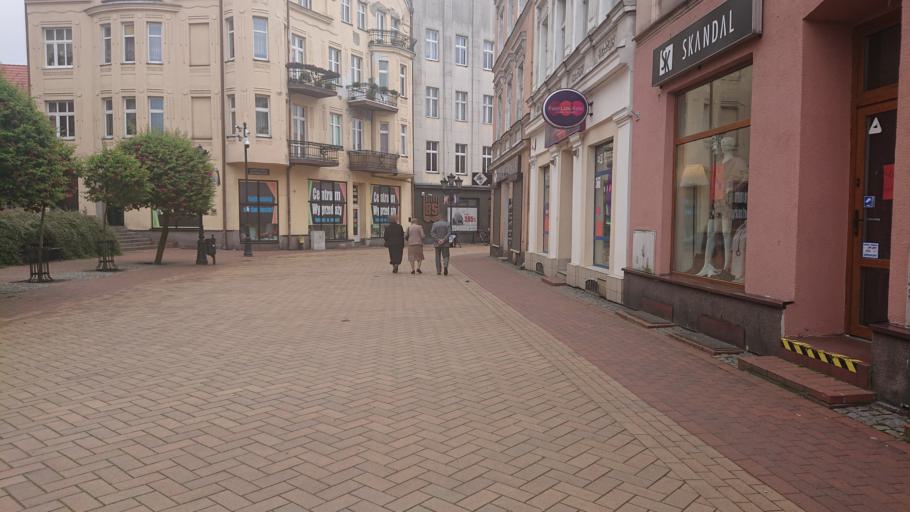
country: PL
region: Pomeranian Voivodeship
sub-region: Powiat chojnicki
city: Chojnice
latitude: 53.6949
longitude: 17.5631
